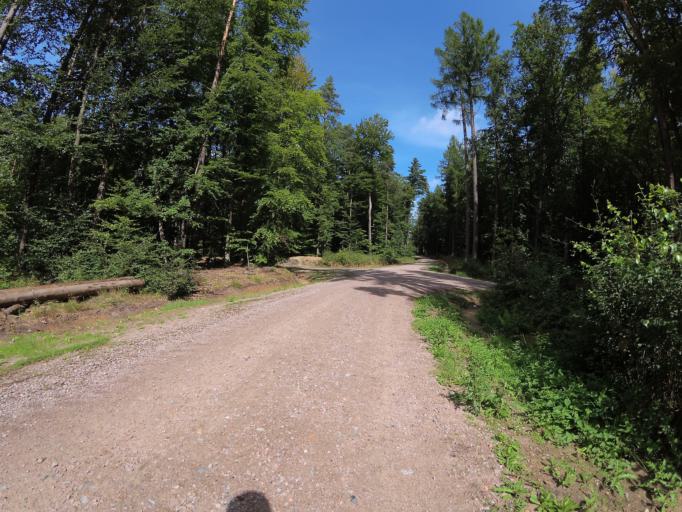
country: PL
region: Pomeranian Voivodeship
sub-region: Powiat wejherowski
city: Bojano
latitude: 54.5120
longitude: 18.4225
